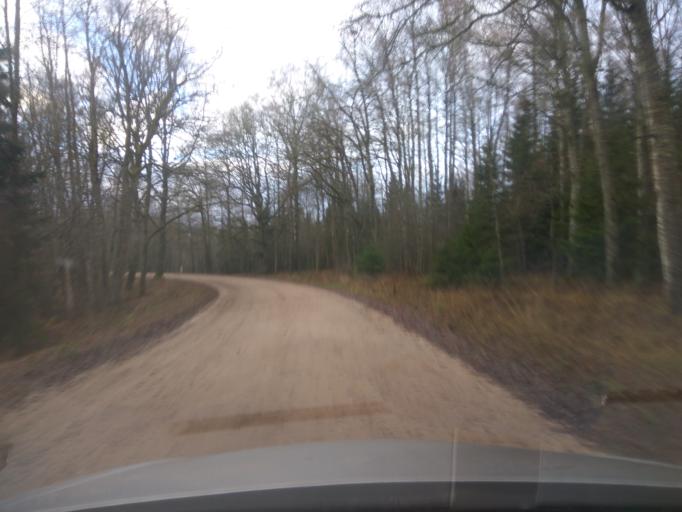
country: LV
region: Kuldigas Rajons
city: Kuldiga
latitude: 56.8347
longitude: 21.8244
